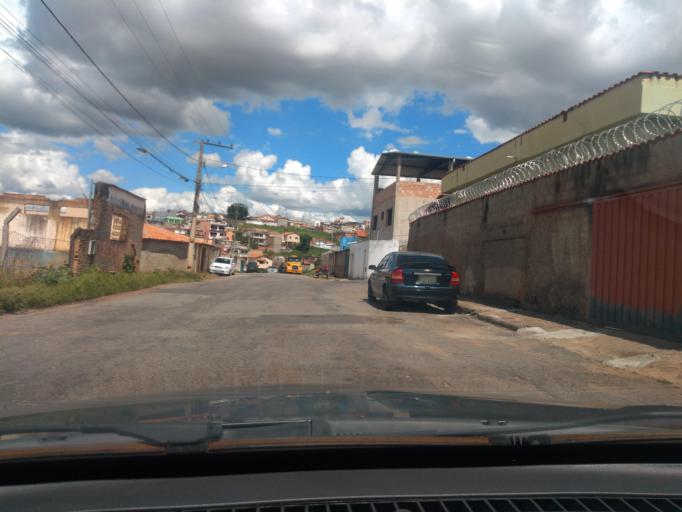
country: BR
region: Minas Gerais
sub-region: Tres Coracoes
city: Tres Coracoes
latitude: -21.6831
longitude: -45.2533
